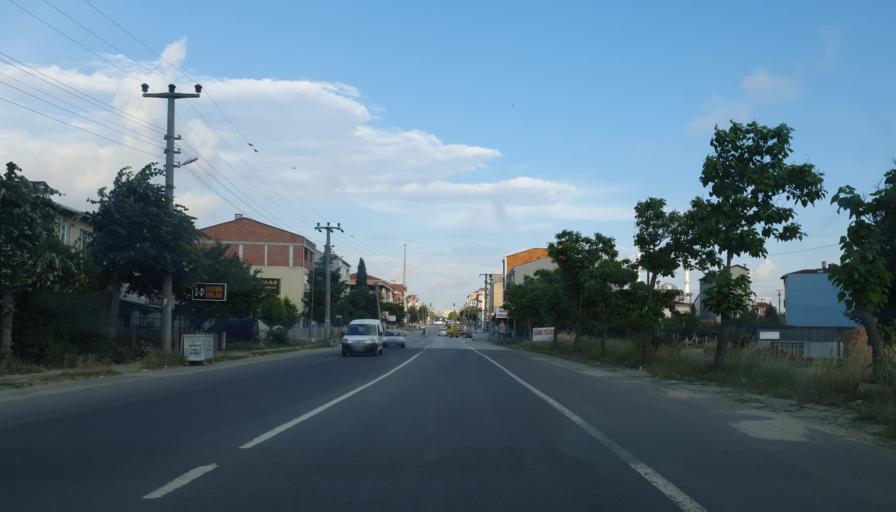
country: TR
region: Tekirdag
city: Saray
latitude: 41.3603
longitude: 27.9451
